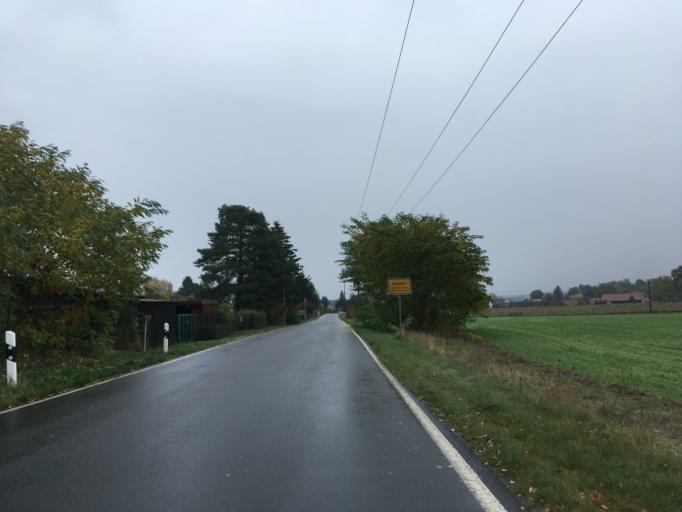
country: DE
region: Brandenburg
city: Neu Zauche
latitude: 52.0169
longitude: 14.1691
